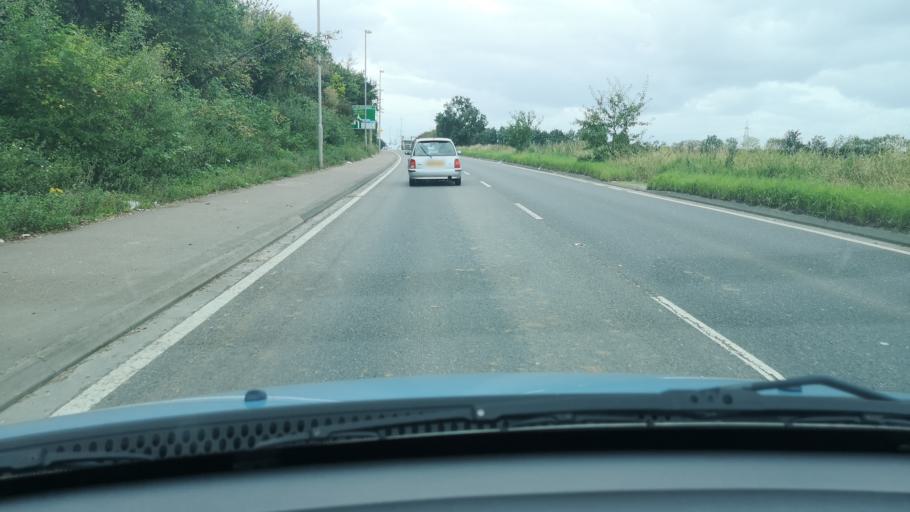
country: GB
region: England
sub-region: City and Borough of Wakefield
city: North Elmsall
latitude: 53.6056
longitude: -1.2726
